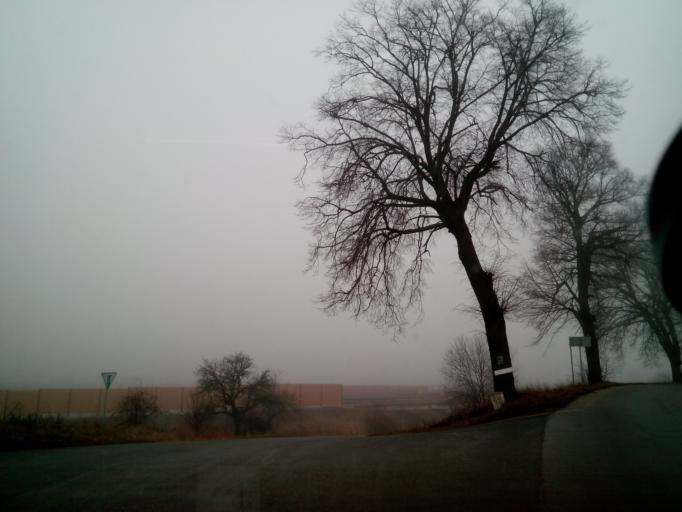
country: SK
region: Presovsky
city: Spisske Podhradie
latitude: 49.0066
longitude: 20.7627
